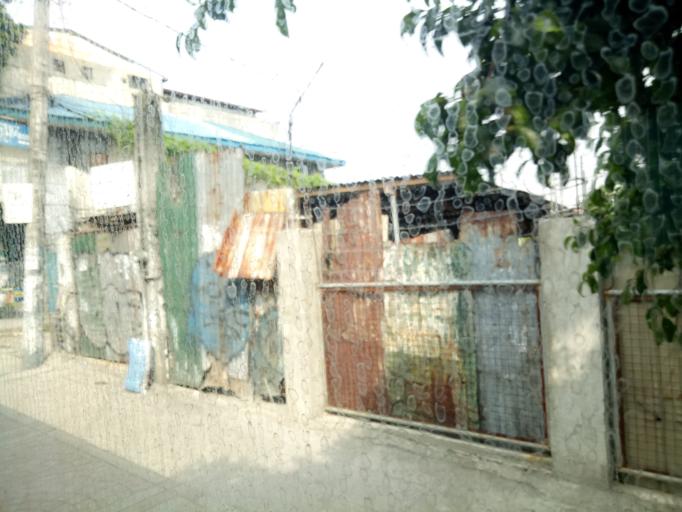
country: PH
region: Calabarzon
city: Bagong Pagasa
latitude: 14.7064
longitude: 121.0384
